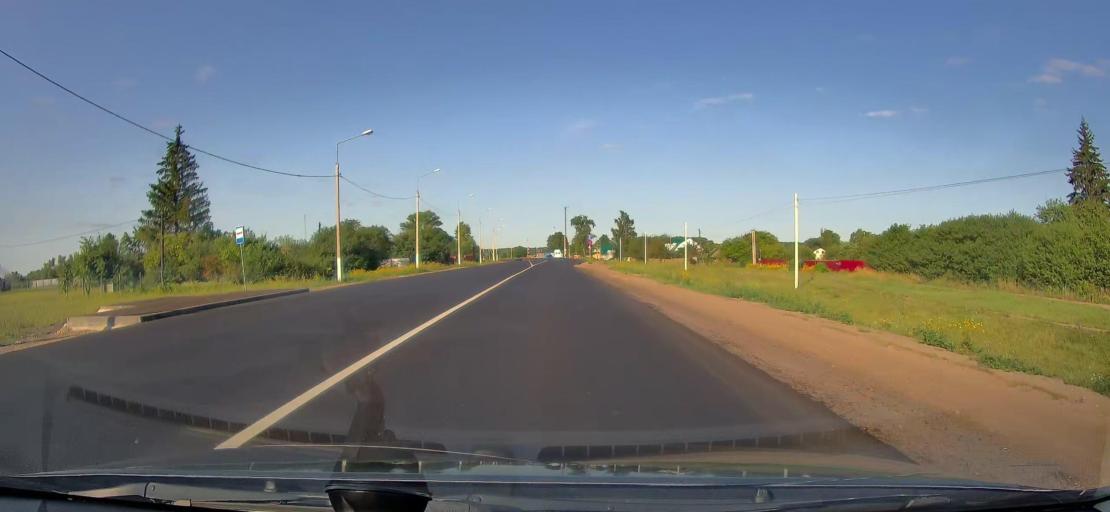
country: RU
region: Tula
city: Bol'shoye Skuratovo
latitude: 53.4331
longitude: 36.8036
